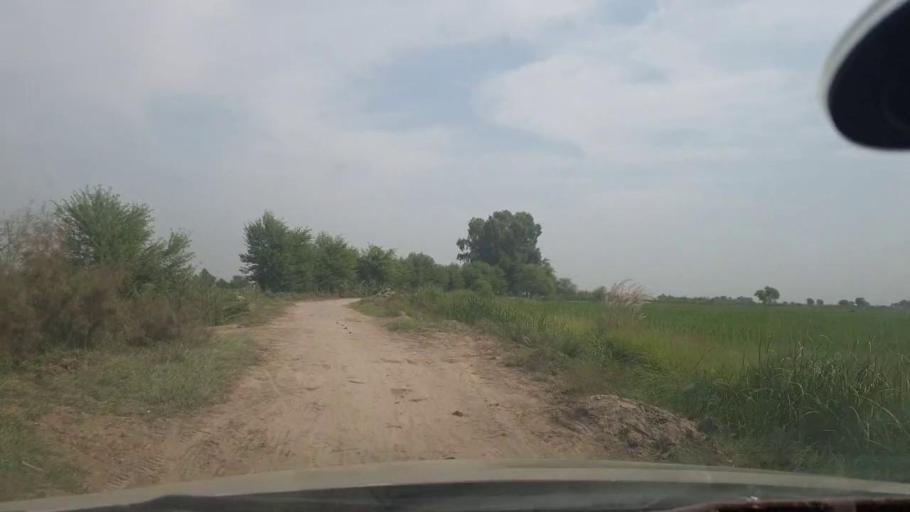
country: PK
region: Sindh
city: Jacobabad
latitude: 28.3158
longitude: 68.4826
